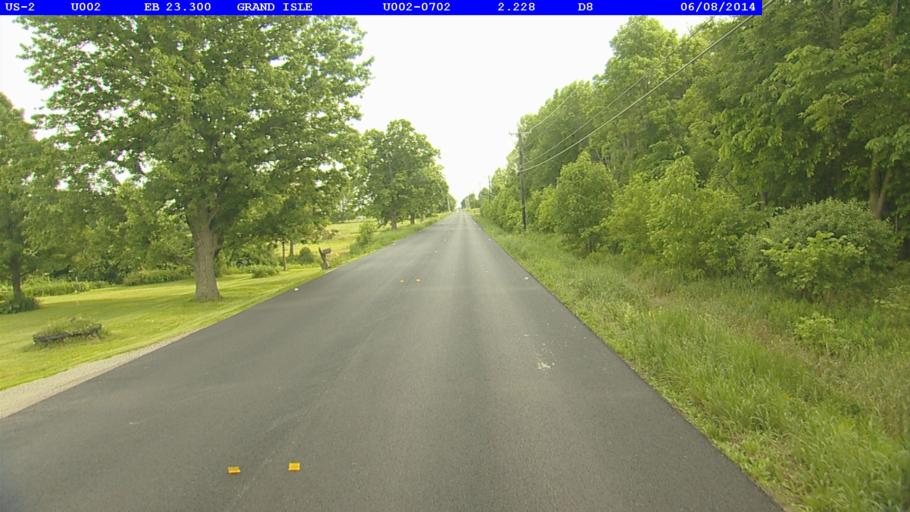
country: US
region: Vermont
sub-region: Grand Isle County
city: North Hero
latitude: 44.7353
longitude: -73.2907
